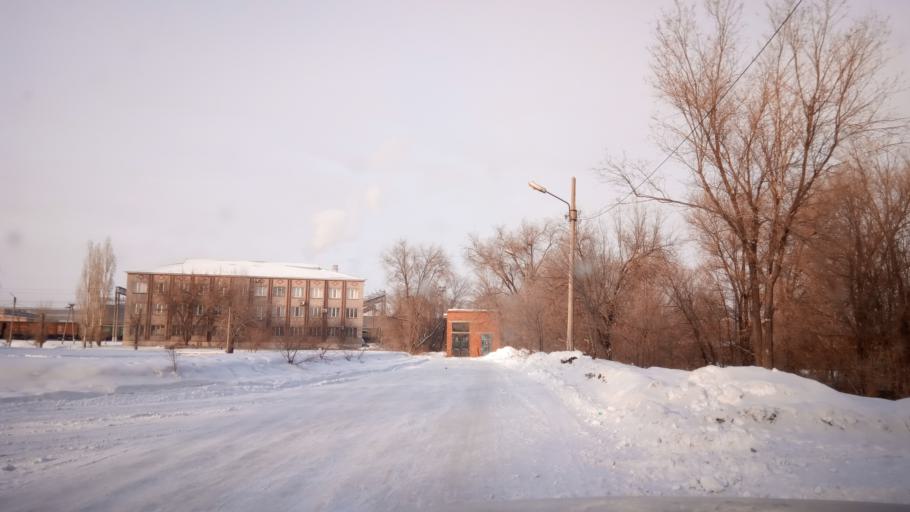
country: RU
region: Orenburg
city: Novotroitsk
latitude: 51.2033
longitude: 58.3481
